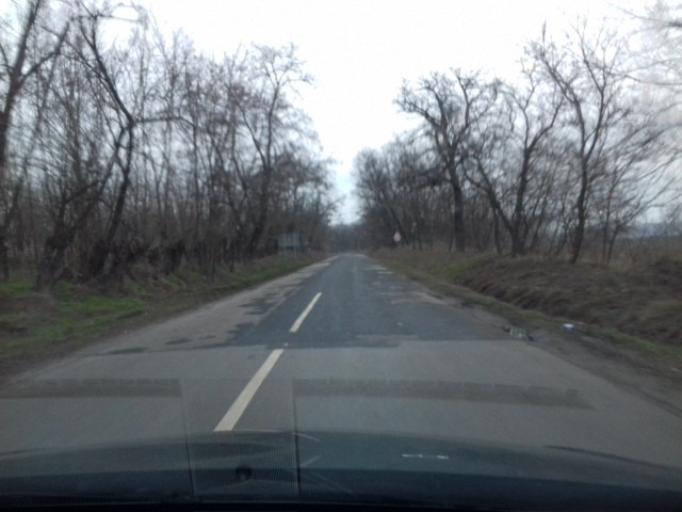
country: HU
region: Szabolcs-Szatmar-Bereg
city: Nyirbogdany
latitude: 48.0645
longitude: 21.8604
